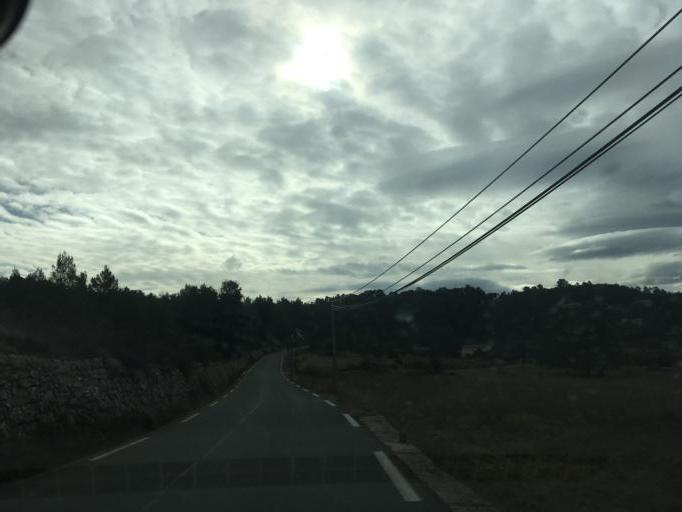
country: FR
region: Provence-Alpes-Cote d'Azur
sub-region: Departement du Var
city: Bras
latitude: 43.4659
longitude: 5.9634
